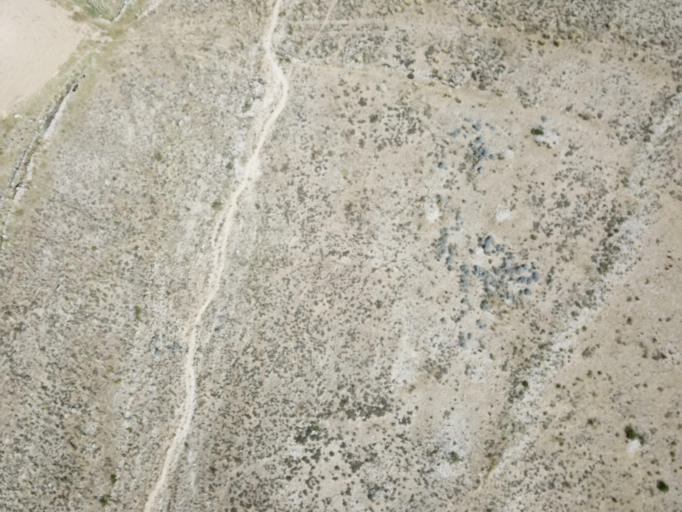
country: BO
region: La Paz
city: Achacachi
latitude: -16.0525
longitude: -68.8105
